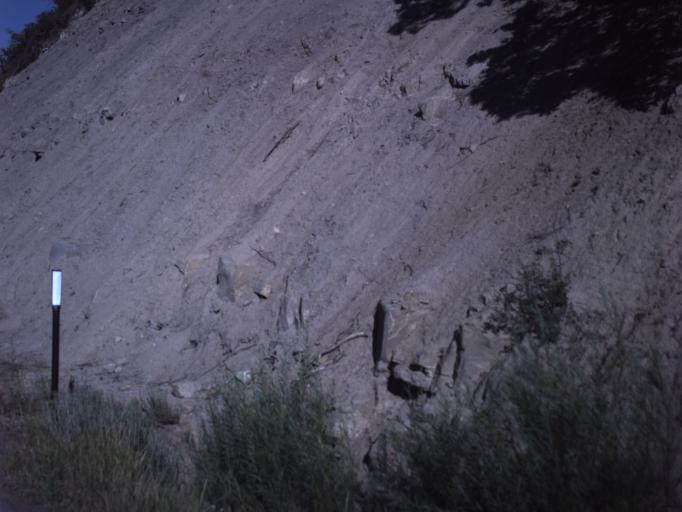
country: US
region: Utah
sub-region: Sanpete County
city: Fairview
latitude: 39.6478
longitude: -111.3712
